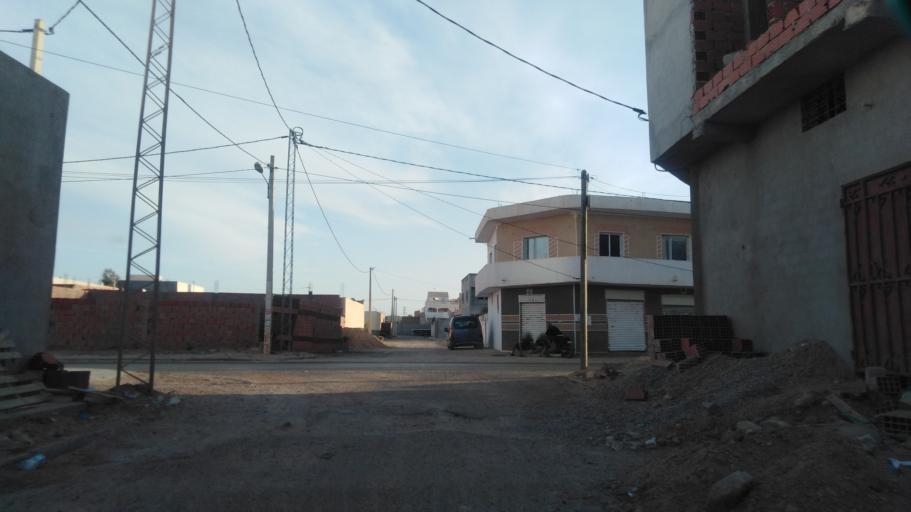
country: TN
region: Tataouine
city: Tataouine
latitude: 32.9529
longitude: 10.4667
